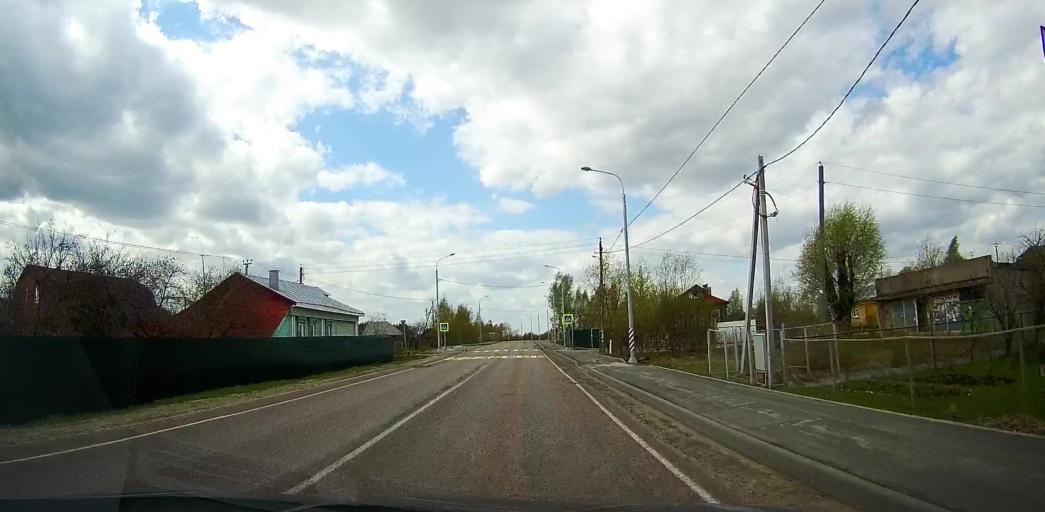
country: RU
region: Moskovskaya
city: Davydovo
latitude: 55.6647
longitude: 38.8010
